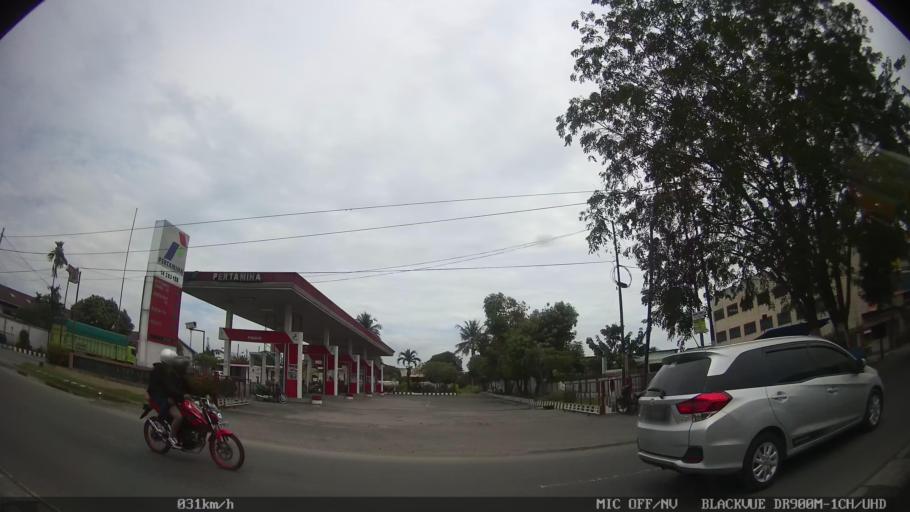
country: ID
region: North Sumatra
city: Sunggal
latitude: 3.5990
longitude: 98.5743
